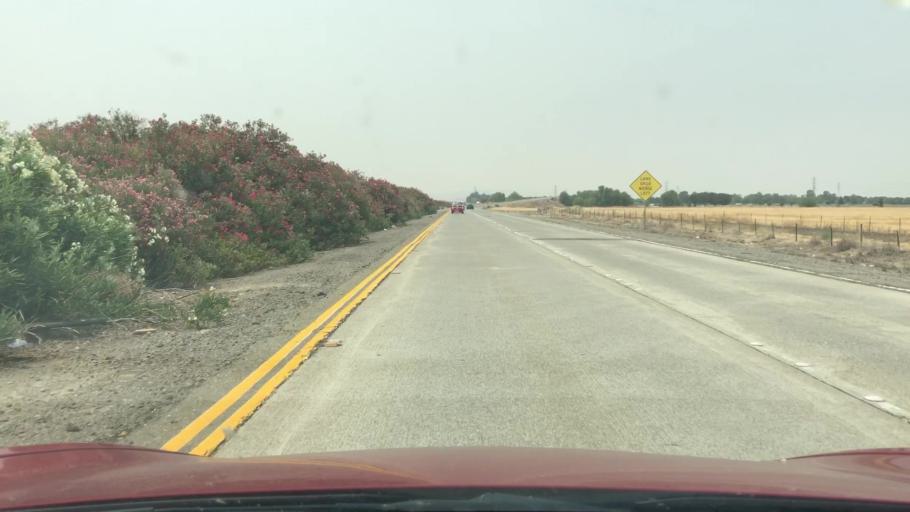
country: US
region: California
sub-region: San Joaquin County
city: Tracy
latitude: 37.7397
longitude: -121.4867
